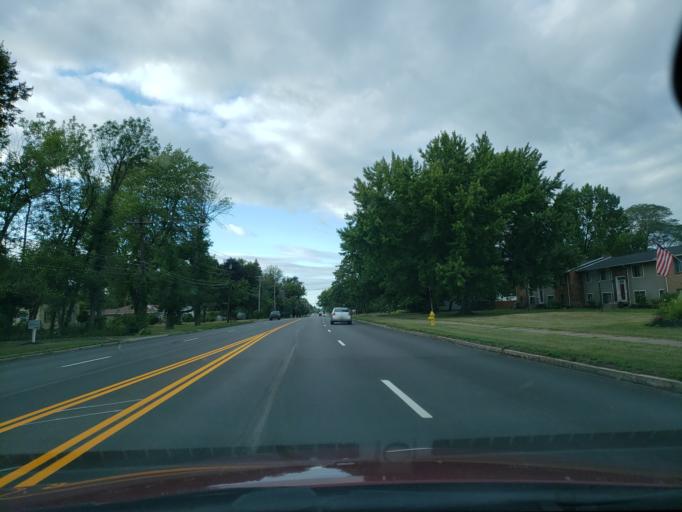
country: US
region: New York
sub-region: Monroe County
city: Greece
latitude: 43.2321
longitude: -77.6591
